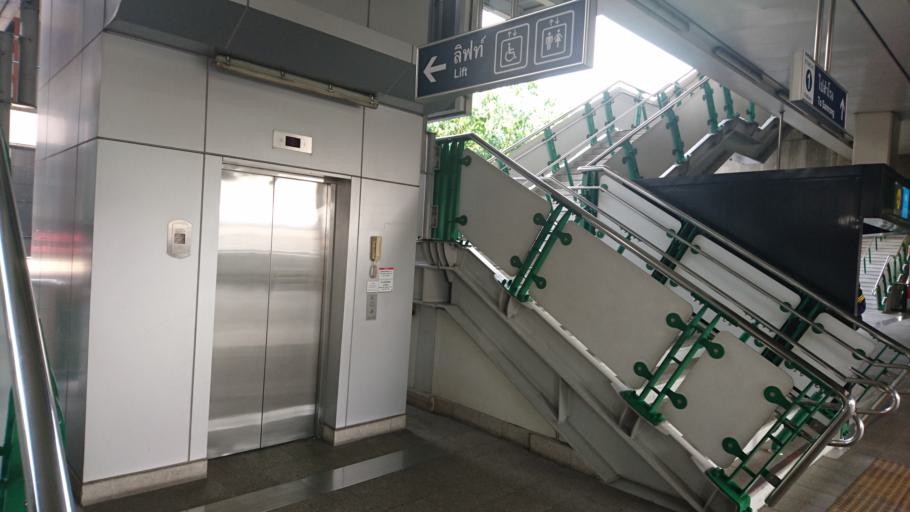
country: TH
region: Bangkok
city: Phra Khanong
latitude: 13.6799
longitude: 100.6095
